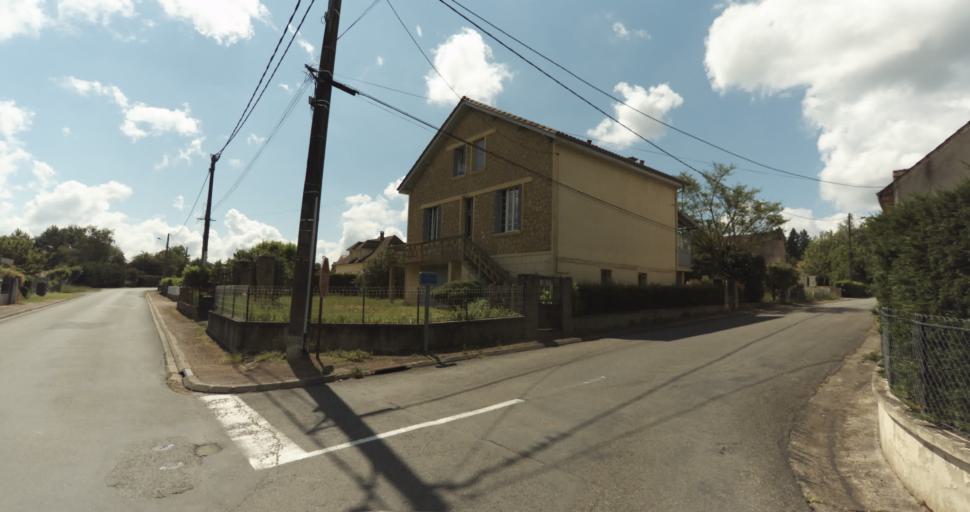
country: FR
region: Aquitaine
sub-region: Departement de la Dordogne
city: Le Bugue
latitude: 44.8432
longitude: 0.9110
